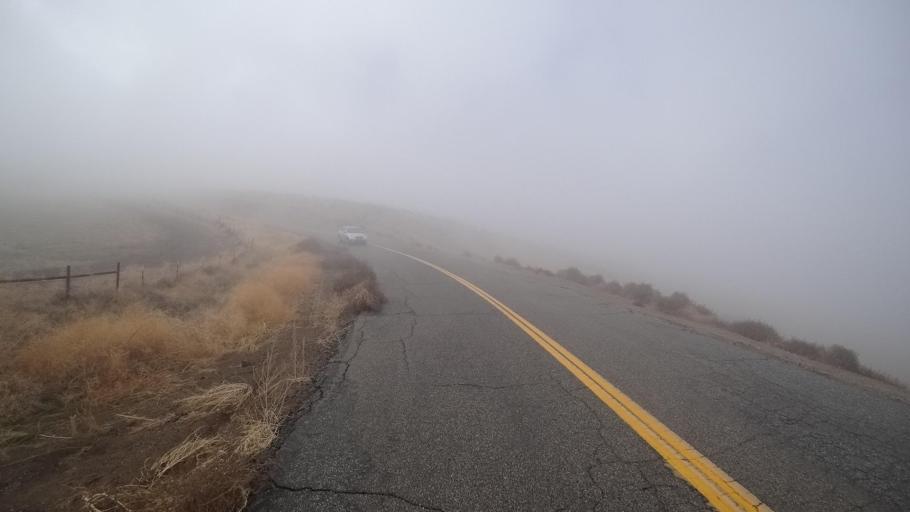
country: US
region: California
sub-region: Kern County
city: Maricopa
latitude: 34.9343
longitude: -119.4138
